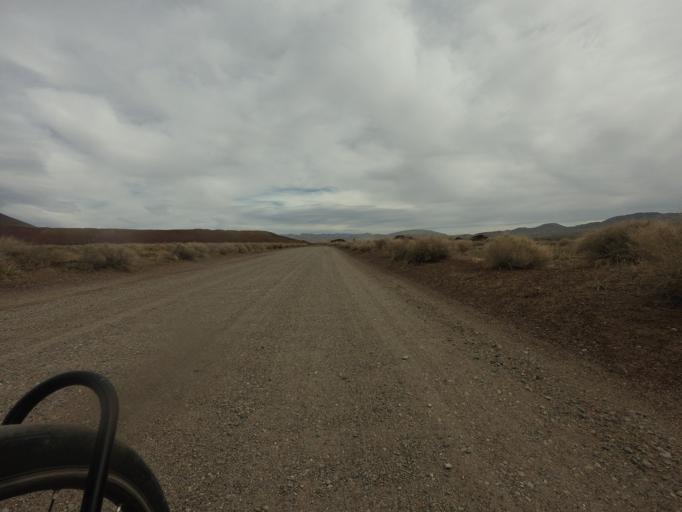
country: US
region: California
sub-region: Kern County
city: Inyokern
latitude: 35.9768
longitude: -117.9137
